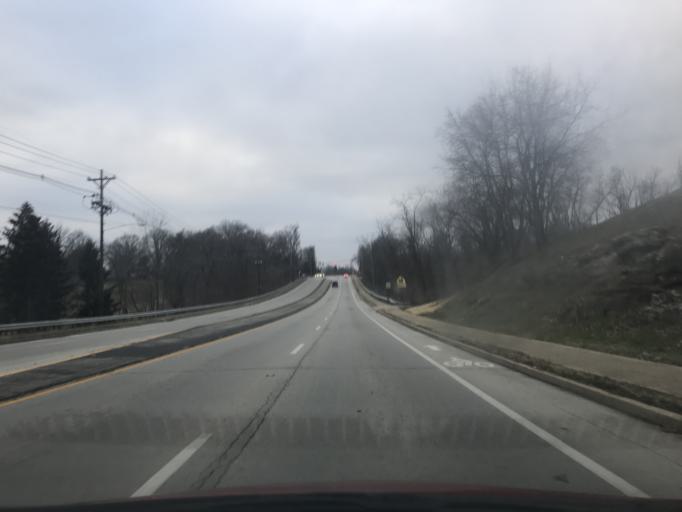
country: US
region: Kentucky
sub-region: Jefferson County
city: Audubon Park
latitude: 38.2156
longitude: -85.7246
